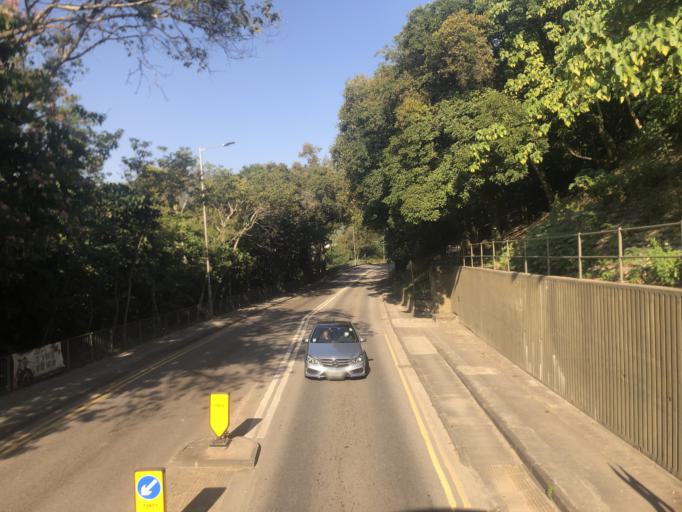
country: CN
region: Guangdong
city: Liantang
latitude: 22.5202
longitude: 114.1766
